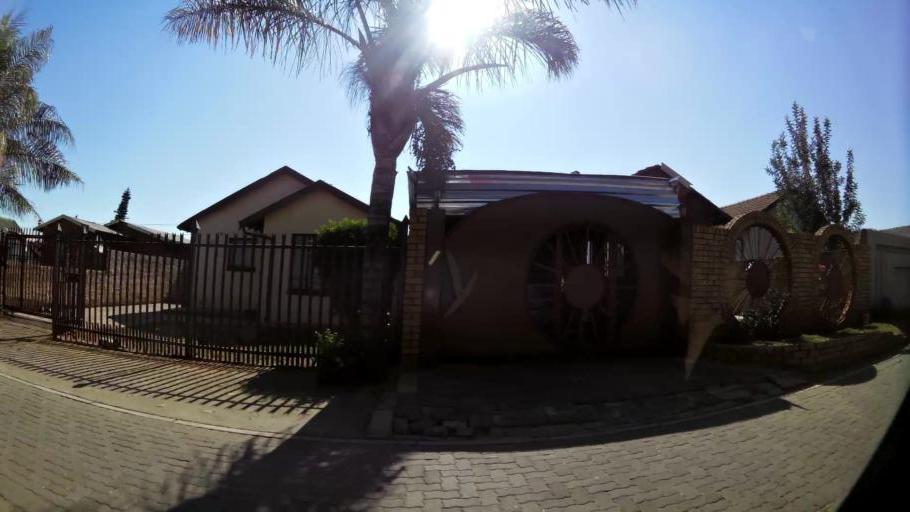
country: ZA
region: Gauteng
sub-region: City of Tshwane Metropolitan Municipality
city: Mabopane
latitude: -25.5562
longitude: 28.0756
